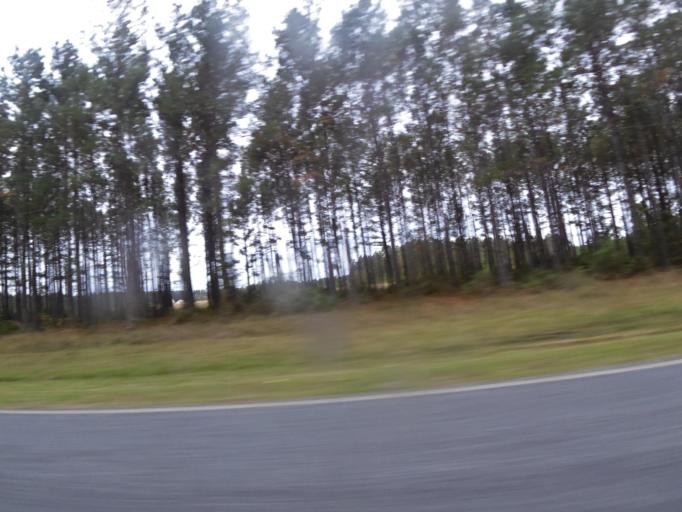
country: US
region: Georgia
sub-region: Charlton County
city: Folkston
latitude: 30.9139
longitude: -82.0832
